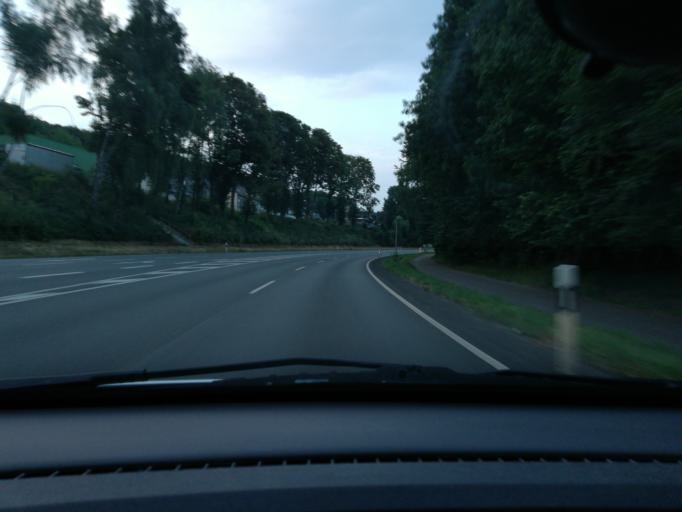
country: DE
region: North Rhine-Westphalia
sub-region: Regierungsbezirk Arnsberg
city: Schwelm
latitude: 51.2905
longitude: 7.2752
